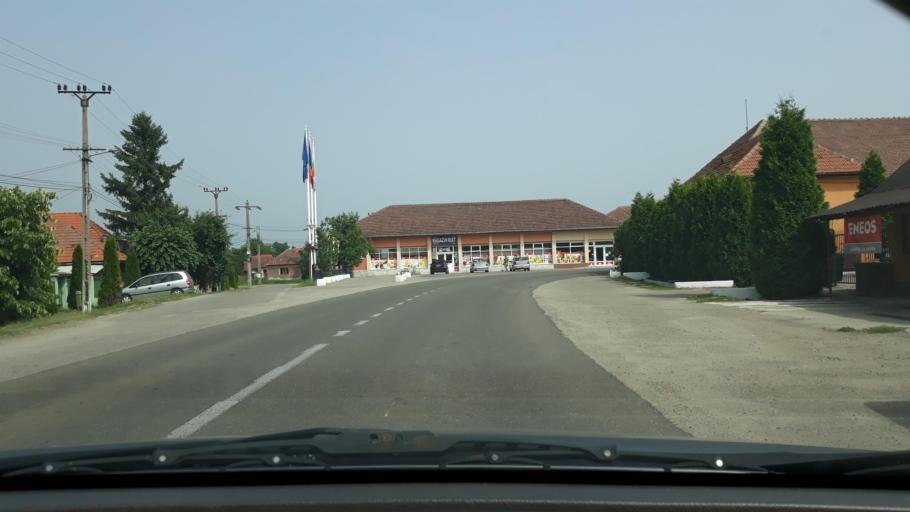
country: RO
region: Bihor
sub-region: Comuna Tauteu
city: Tauteu
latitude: 47.2726
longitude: 22.3367
